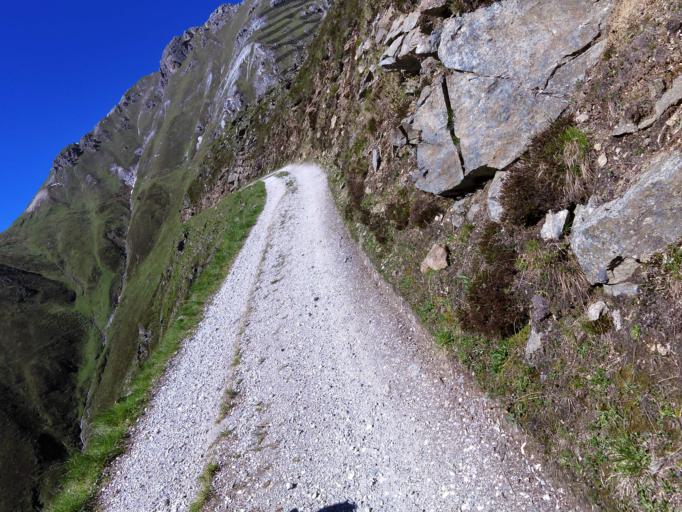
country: AT
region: Tyrol
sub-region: Politischer Bezirk Innsbruck Land
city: Neustift im Stubaital
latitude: 47.1255
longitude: 11.2792
